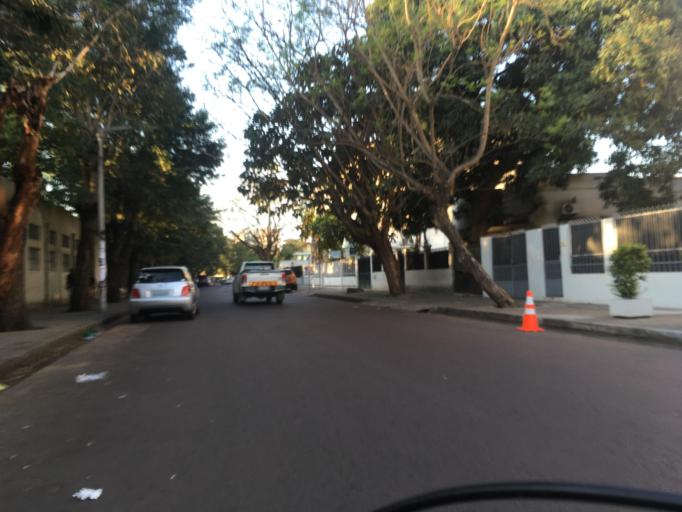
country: MZ
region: Maputo City
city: Maputo
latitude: -25.9712
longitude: 32.5900
